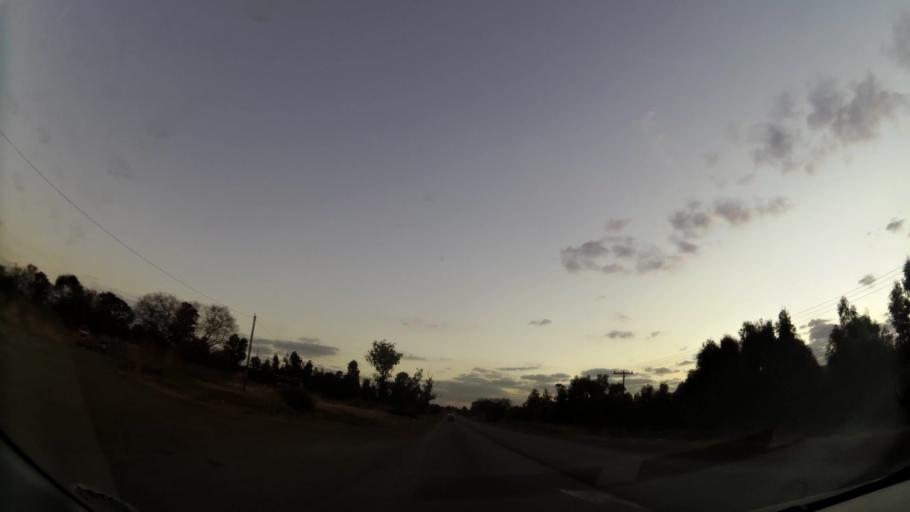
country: ZA
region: Gauteng
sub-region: West Rand District Municipality
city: Krugersdorp
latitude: -26.0647
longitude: 27.6934
